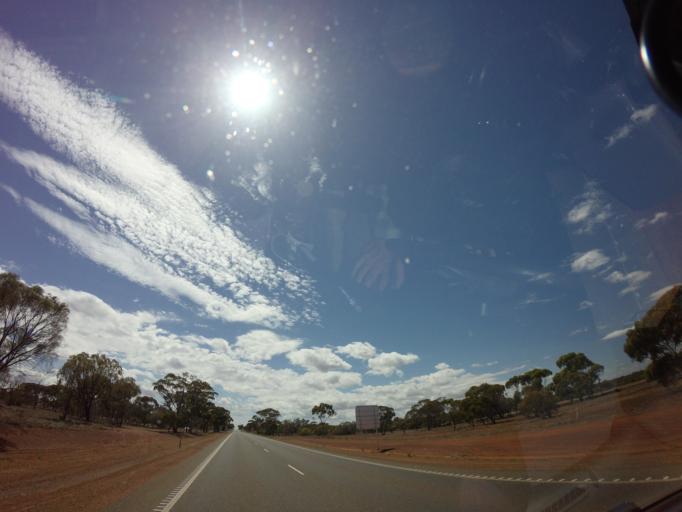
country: AU
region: Western Australia
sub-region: Kalgoorlie/Boulder
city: Boulder
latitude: -30.9546
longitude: 121.1522
